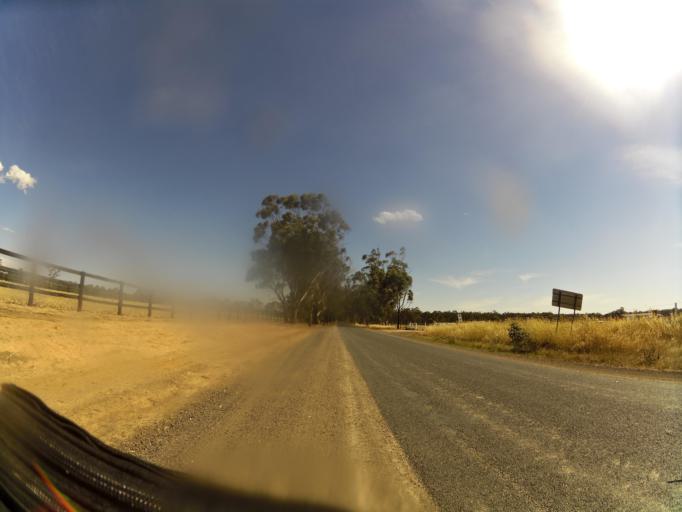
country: AU
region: Victoria
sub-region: Campaspe
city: Kyabram
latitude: -36.8627
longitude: 145.0879
